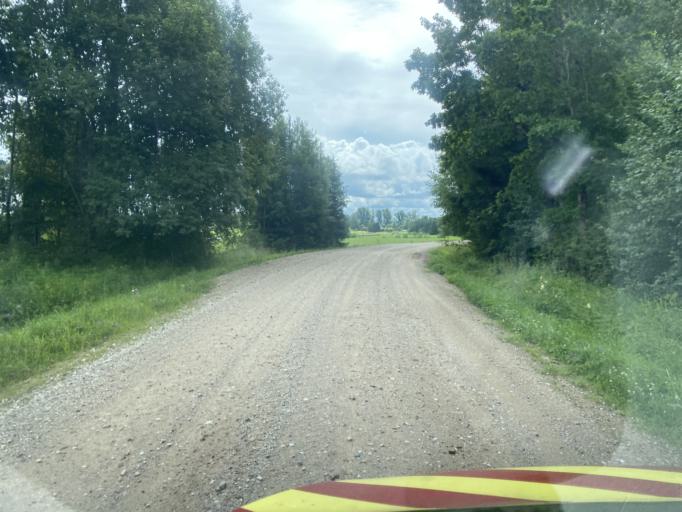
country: EE
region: Viljandimaa
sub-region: Karksi vald
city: Karksi-Nuia
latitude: 58.0599
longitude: 25.5397
